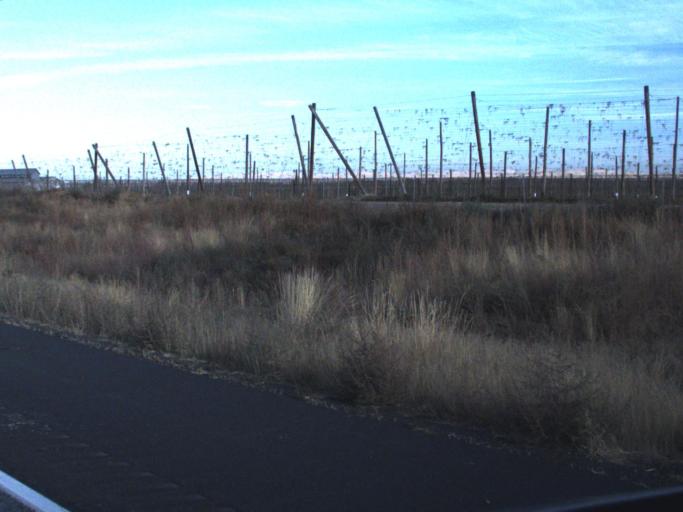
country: US
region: Washington
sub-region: Yakima County
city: Grandview
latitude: 46.2494
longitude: -119.8607
